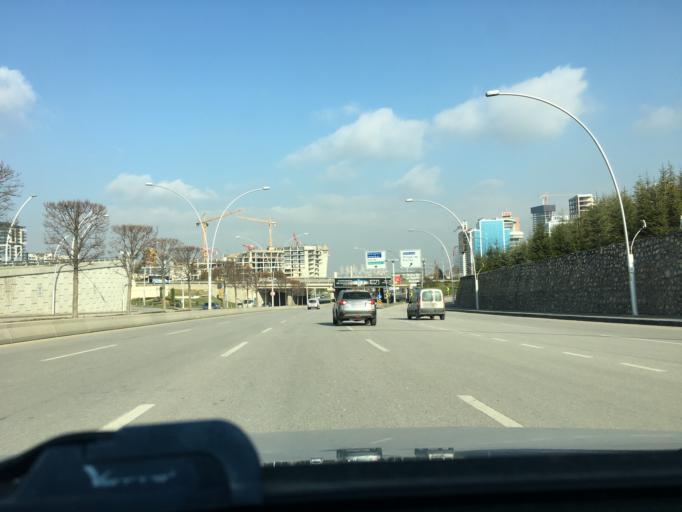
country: TR
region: Ankara
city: Ankara
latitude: 39.9067
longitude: 32.7866
